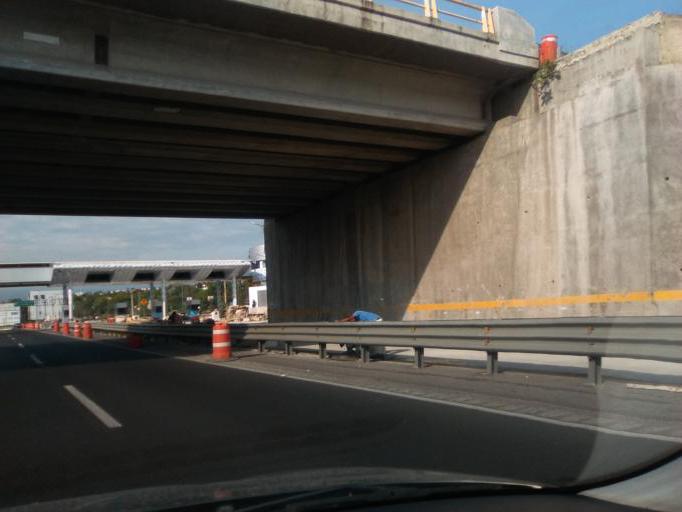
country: MX
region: Morelos
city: Temixco
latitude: 18.8372
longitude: -99.2171
